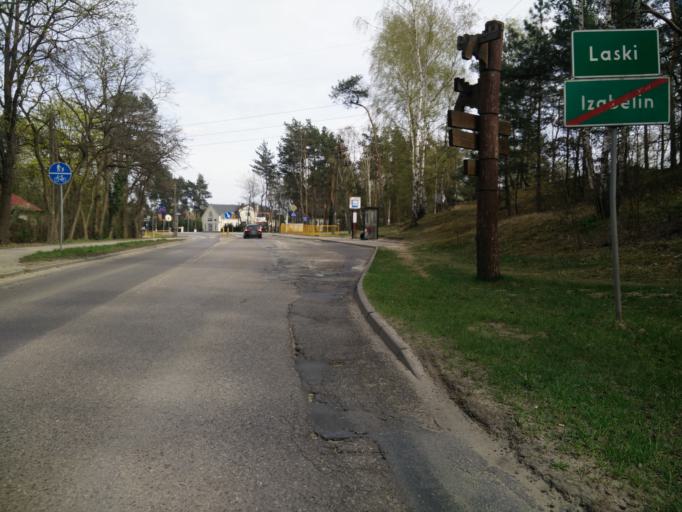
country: PL
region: Masovian Voivodeship
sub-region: Powiat warszawski zachodni
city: Izabelin
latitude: 52.2911
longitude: 20.8381
